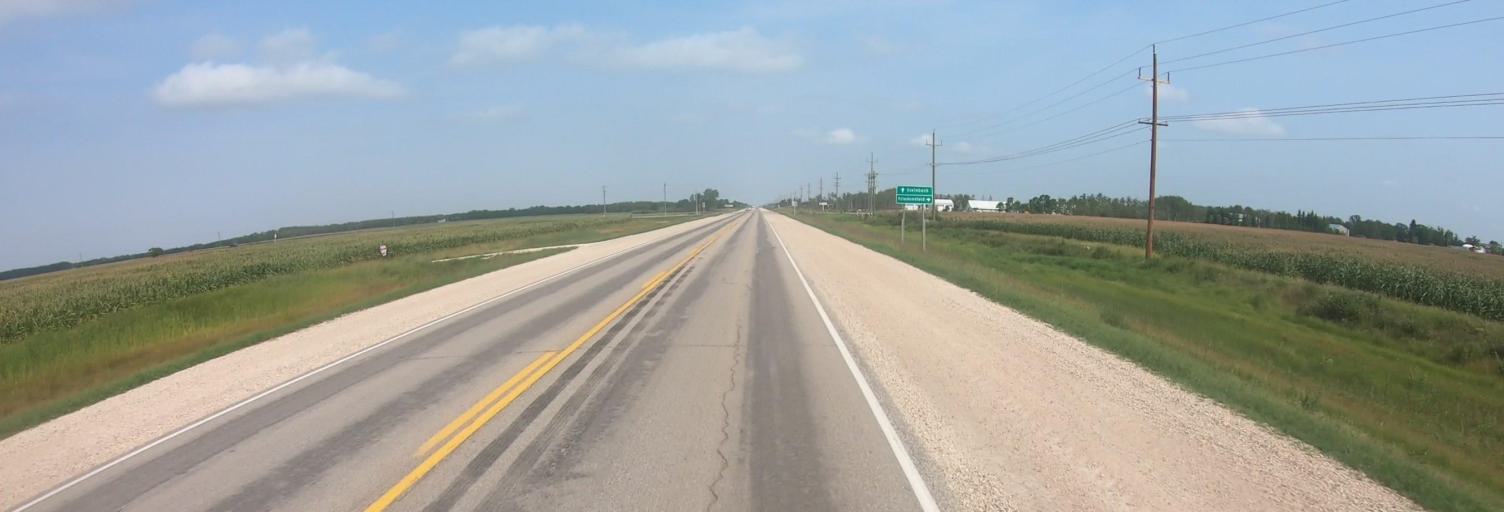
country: CA
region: Manitoba
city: Steinbach
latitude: 49.4709
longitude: -96.6911
